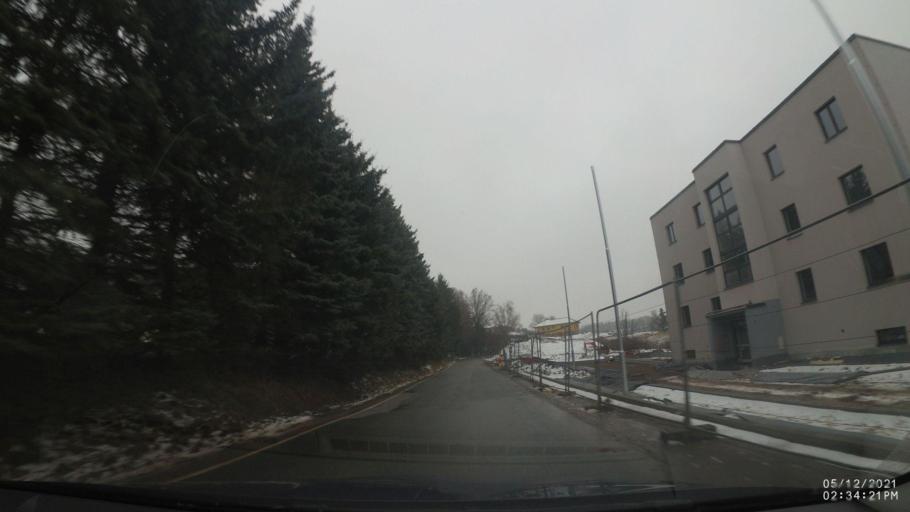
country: CZ
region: Kralovehradecky
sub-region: Okres Nachod
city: Nachod
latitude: 50.4052
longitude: 16.1668
